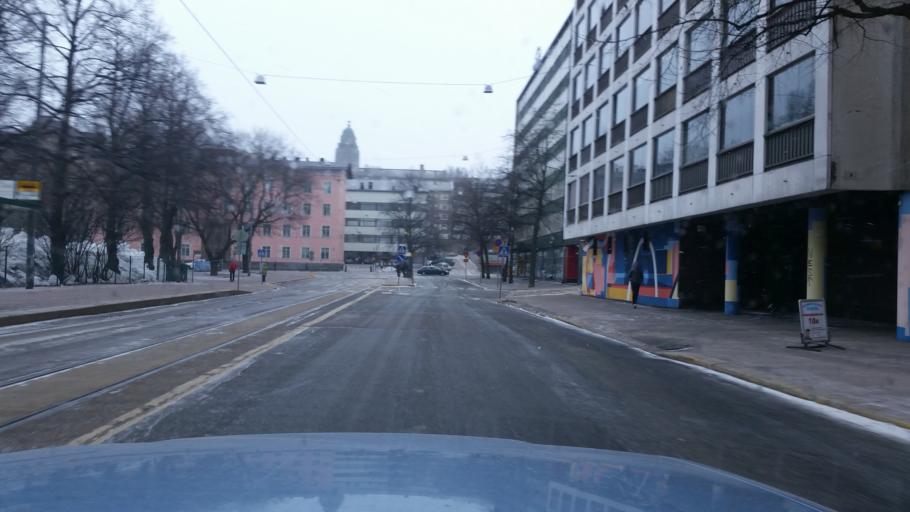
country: FI
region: Uusimaa
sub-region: Helsinki
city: Helsinki
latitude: 60.1876
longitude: 24.9483
